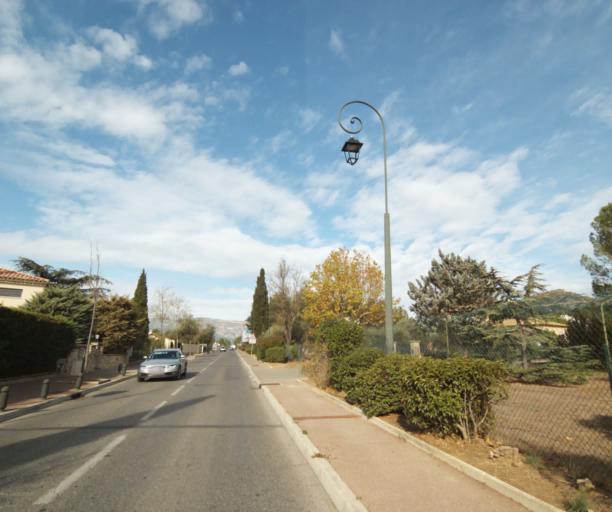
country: FR
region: Provence-Alpes-Cote d'Azur
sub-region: Departement des Bouches-du-Rhone
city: Gemenos
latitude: 43.3000
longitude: 5.6200
